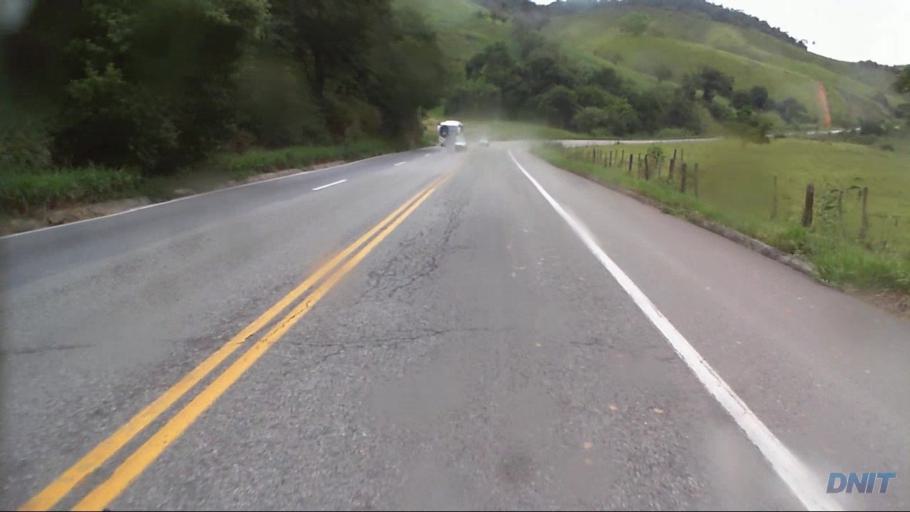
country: BR
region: Minas Gerais
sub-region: Nova Era
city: Nova Era
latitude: -19.7114
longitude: -43.0004
